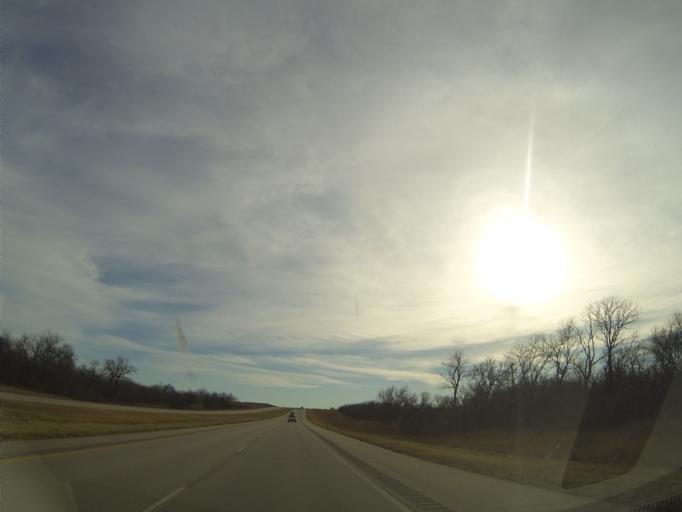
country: US
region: Kansas
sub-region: Ottawa County
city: Minneapolis
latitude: 39.1898
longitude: -97.6677
